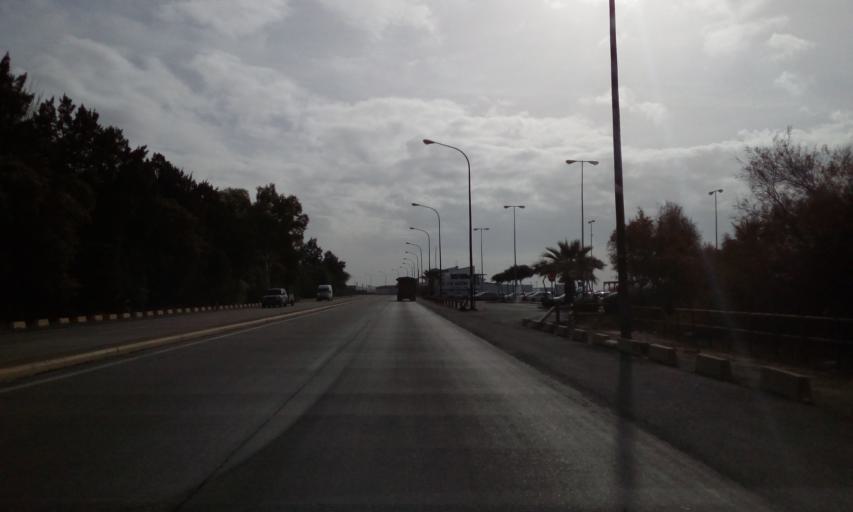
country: ES
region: Andalusia
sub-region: Provincia de Huelva
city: Punta Umbria
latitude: 37.2184
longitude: -6.9478
